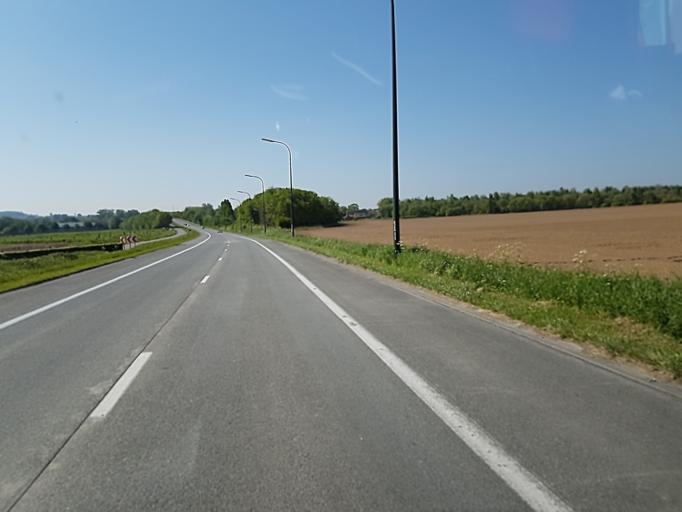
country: BE
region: Wallonia
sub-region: Province du Hainaut
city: Ath
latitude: 50.6724
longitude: 3.7978
